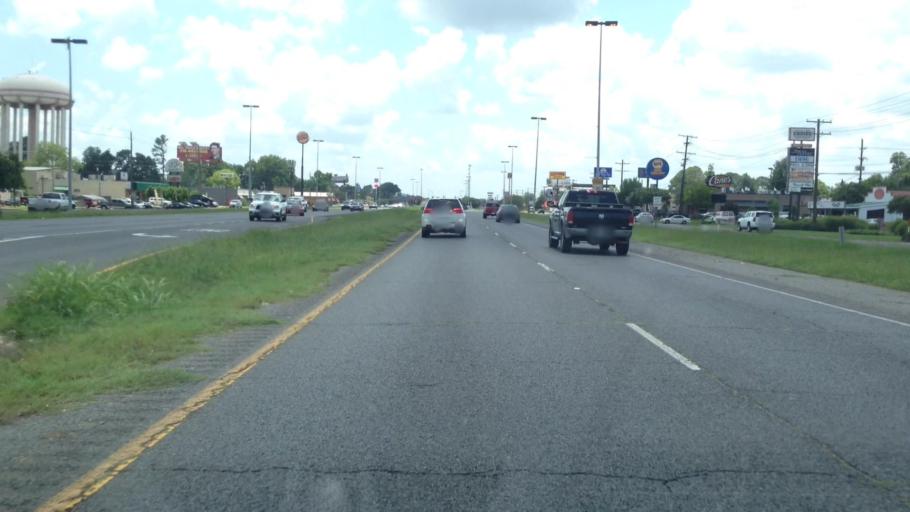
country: US
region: Louisiana
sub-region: Rapides Parish
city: Alexandria
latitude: 31.2926
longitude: -92.4775
